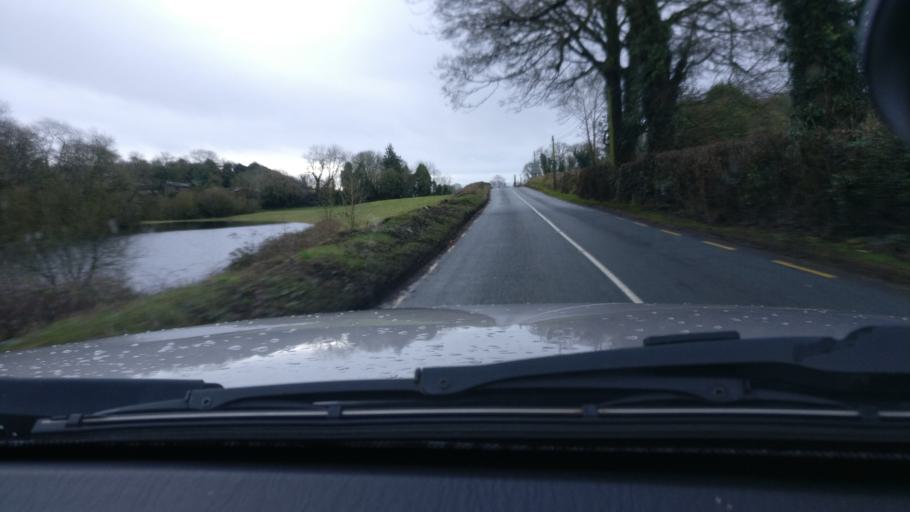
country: IE
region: Leinster
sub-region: An Longfort
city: Granard
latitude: 53.8017
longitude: -7.3889
